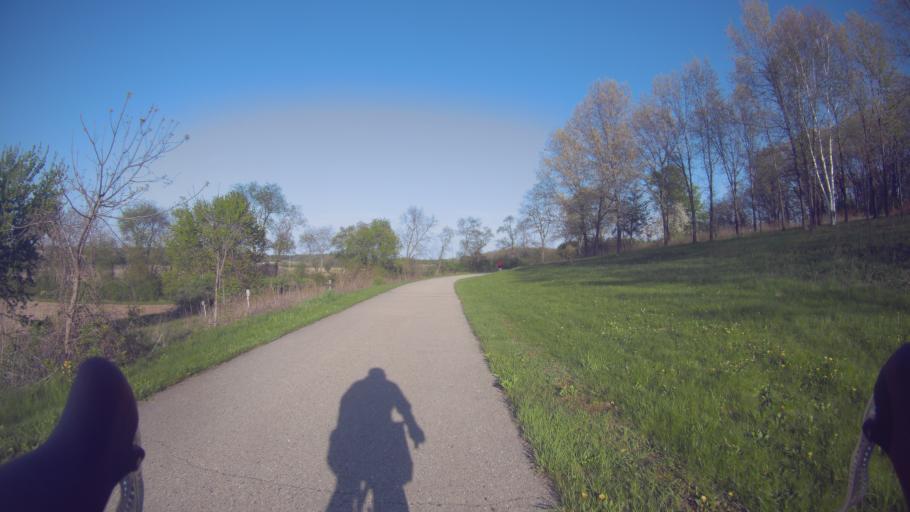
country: US
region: Wisconsin
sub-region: Dane County
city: Monona
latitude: 43.0236
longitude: -89.3728
